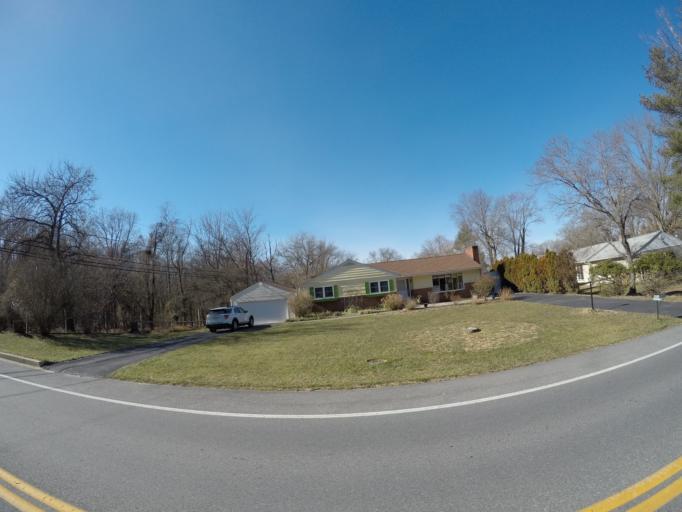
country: US
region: Maryland
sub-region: Howard County
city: Columbia
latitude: 39.2407
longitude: -76.8311
